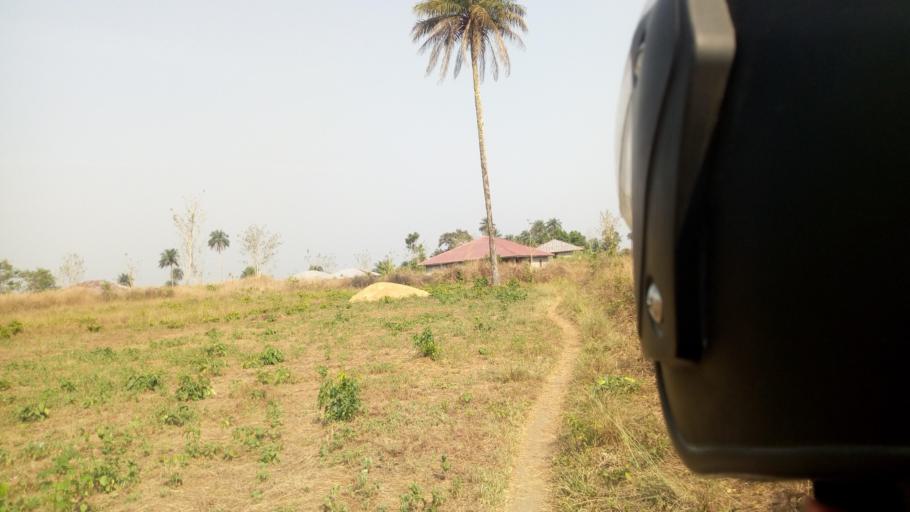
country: SL
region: Southern Province
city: Mogbwemo
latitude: 7.6160
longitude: -12.1769
